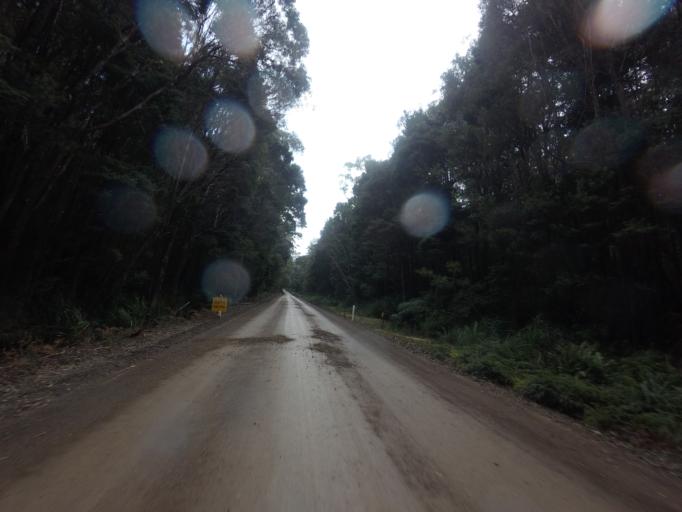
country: AU
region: Tasmania
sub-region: Huon Valley
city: Geeveston
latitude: -43.3962
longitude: 146.8590
